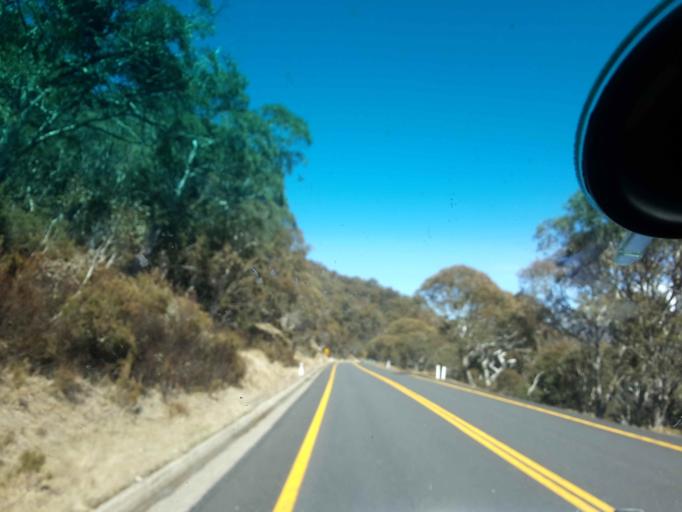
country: AU
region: New South Wales
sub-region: Snowy River
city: Jindabyne
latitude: -36.4934
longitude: 148.3290
